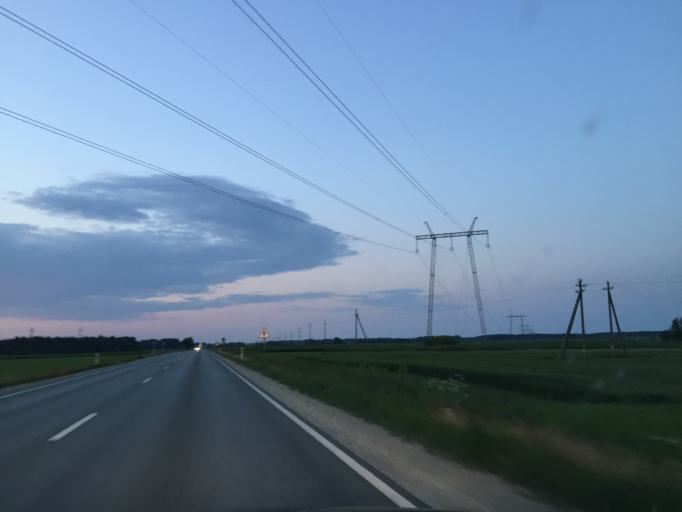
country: LT
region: Siauliu apskritis
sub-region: Joniskis
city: Joniskis
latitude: 56.1080
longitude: 23.4868
